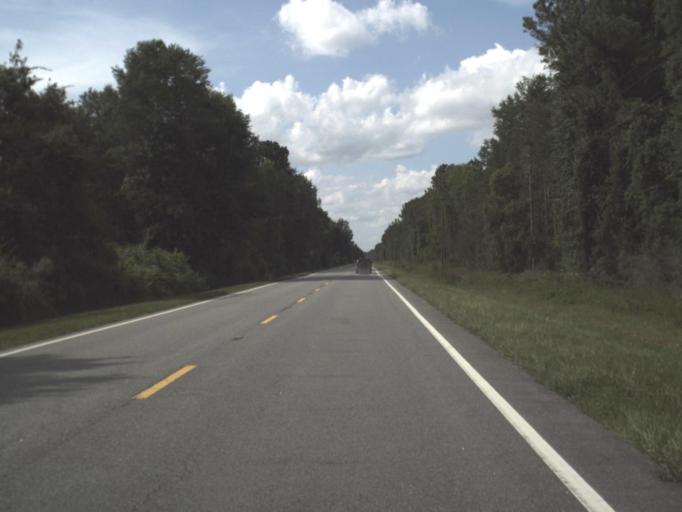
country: US
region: Florida
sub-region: Taylor County
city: Perry
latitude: 30.3189
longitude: -83.6407
